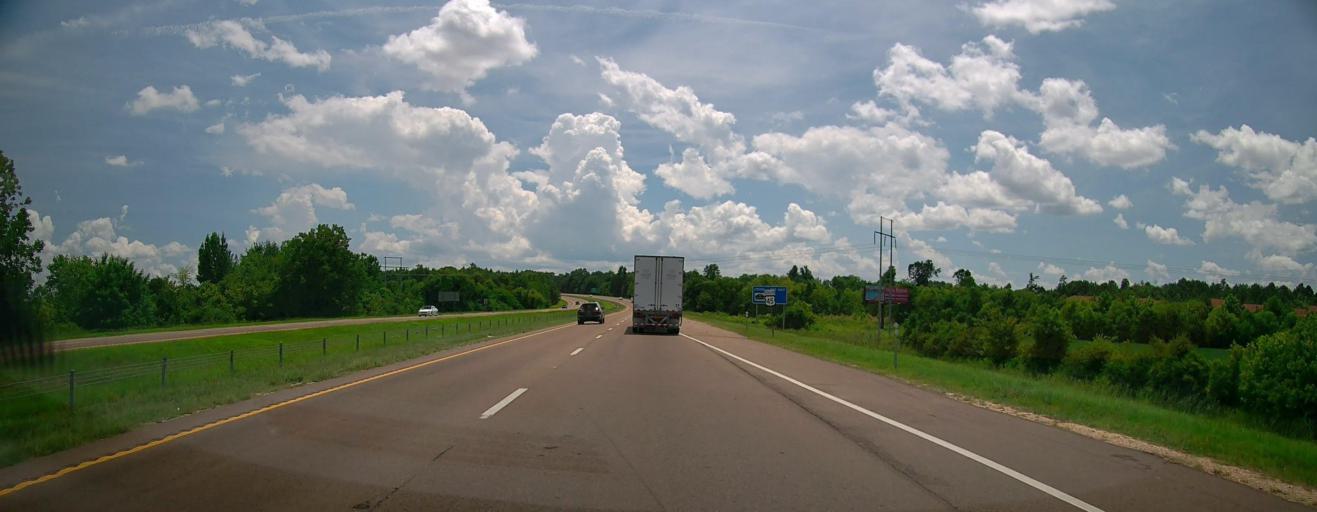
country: US
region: Mississippi
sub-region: Lee County
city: Tupelo
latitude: 34.2890
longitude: -88.7058
